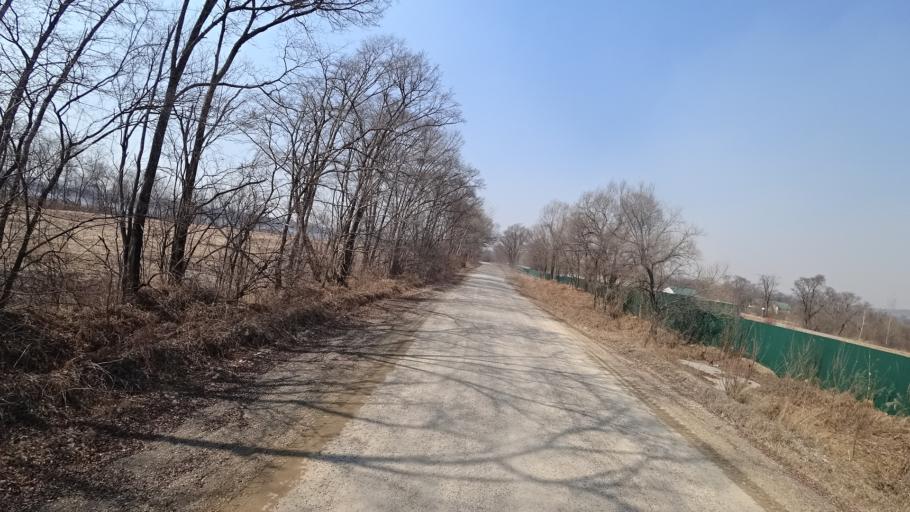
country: RU
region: Amur
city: Novobureyskiy
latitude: 49.7870
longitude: 129.9130
